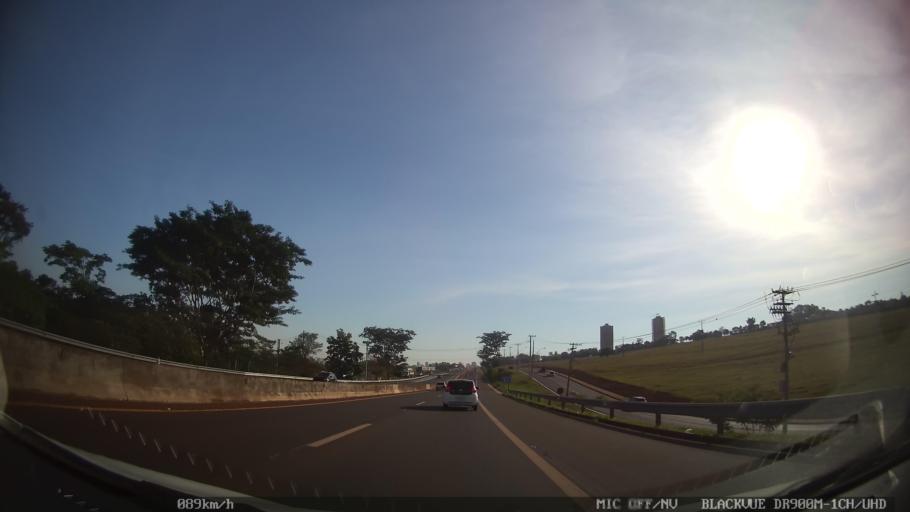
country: BR
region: Sao Paulo
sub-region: Ribeirao Preto
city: Ribeirao Preto
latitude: -21.2487
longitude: -47.8195
